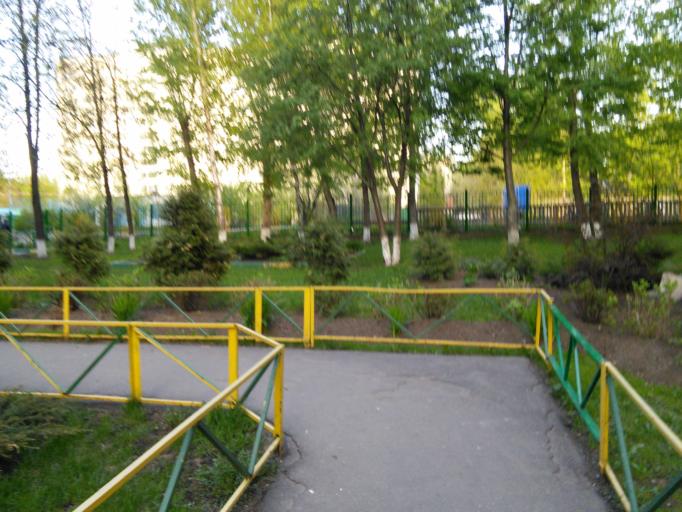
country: RU
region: Moscow
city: Novyye Cheremushki
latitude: 55.6857
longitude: 37.5862
